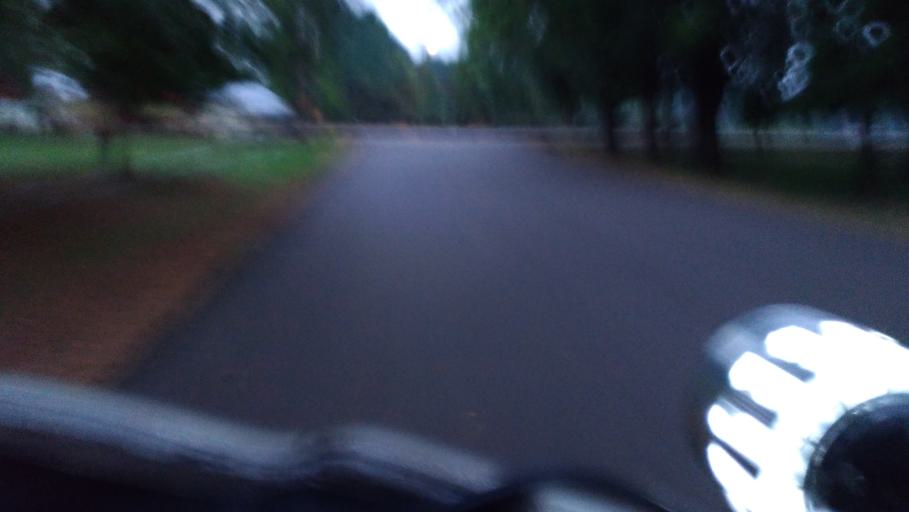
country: ID
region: West Java
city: Cileungsir
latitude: -6.3669
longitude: 106.8986
